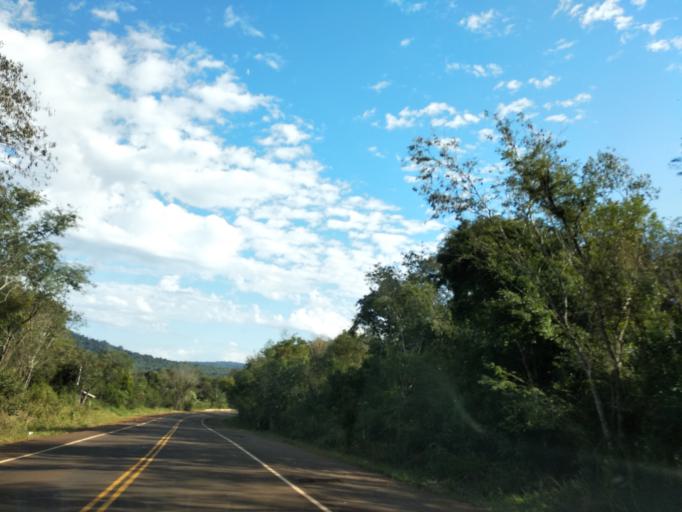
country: AR
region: Misiones
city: Aristobulo del Valle
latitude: -27.1000
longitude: -54.9606
